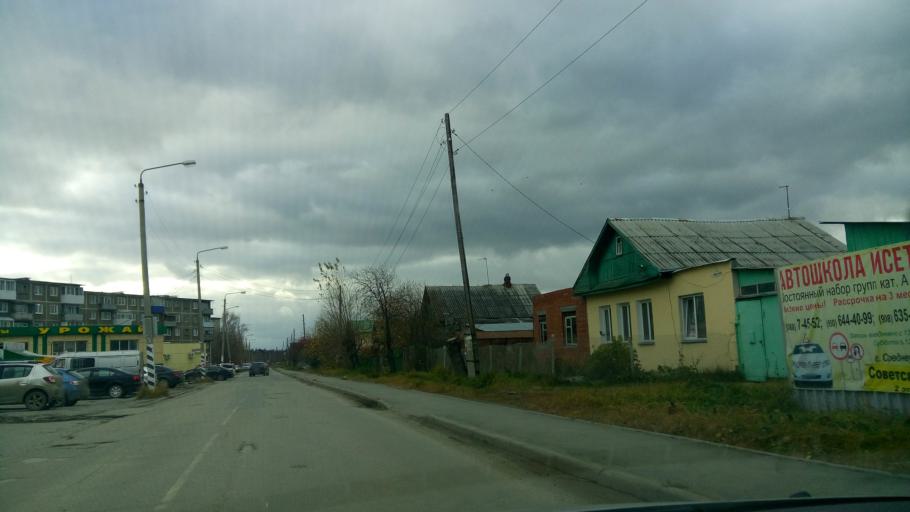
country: RU
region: Sverdlovsk
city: Sredneuralsk
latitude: 56.9840
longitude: 60.4717
